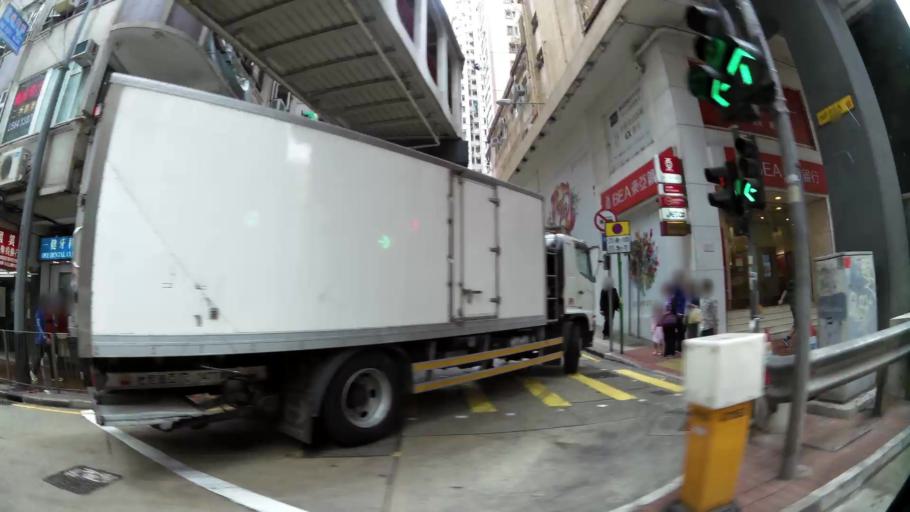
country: HK
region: Wanchai
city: Wan Chai
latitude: 22.2905
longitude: 114.1967
